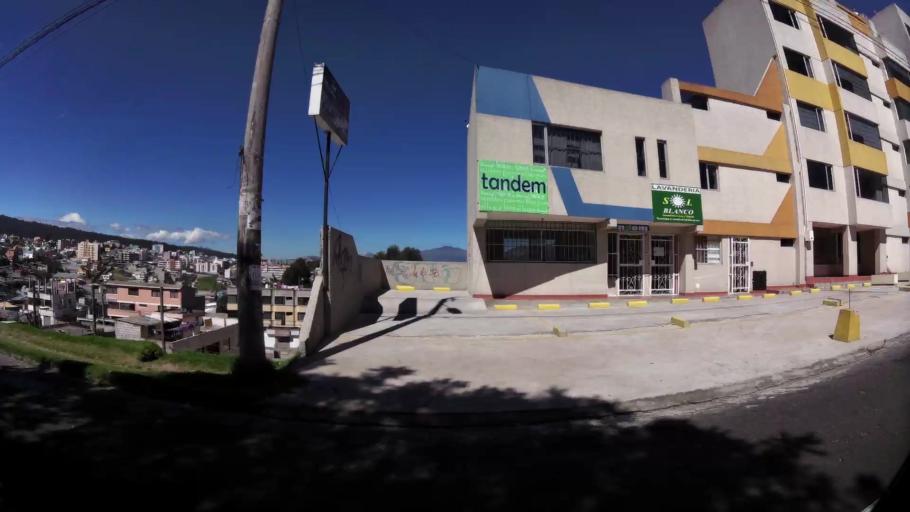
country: EC
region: Pichincha
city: Quito
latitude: -0.1500
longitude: -78.4670
